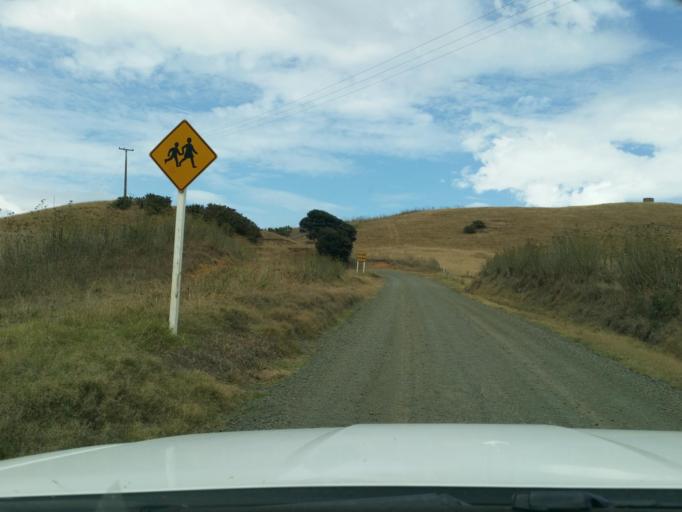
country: NZ
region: Auckland
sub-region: Auckland
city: Wellsford
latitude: -36.3498
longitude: 174.1718
